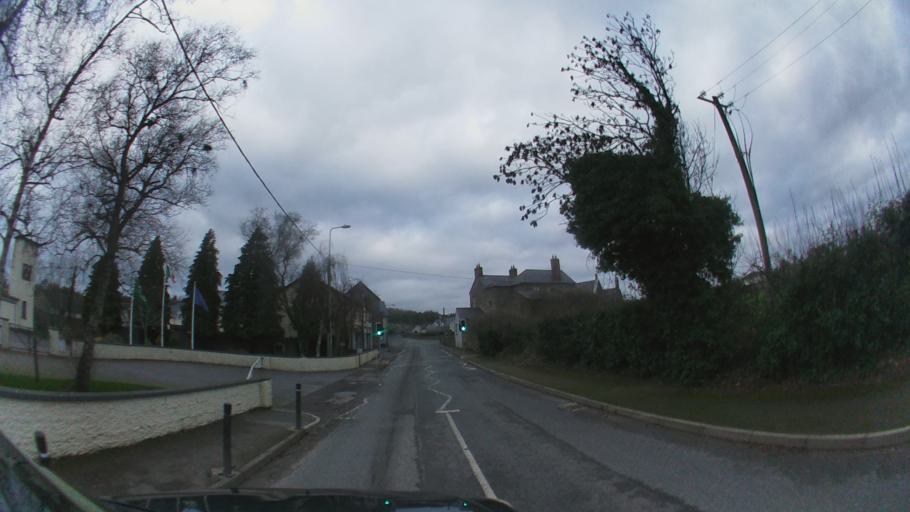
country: IE
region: Leinster
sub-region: An Mhi
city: Duleek
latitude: 53.6913
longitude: -6.4171
